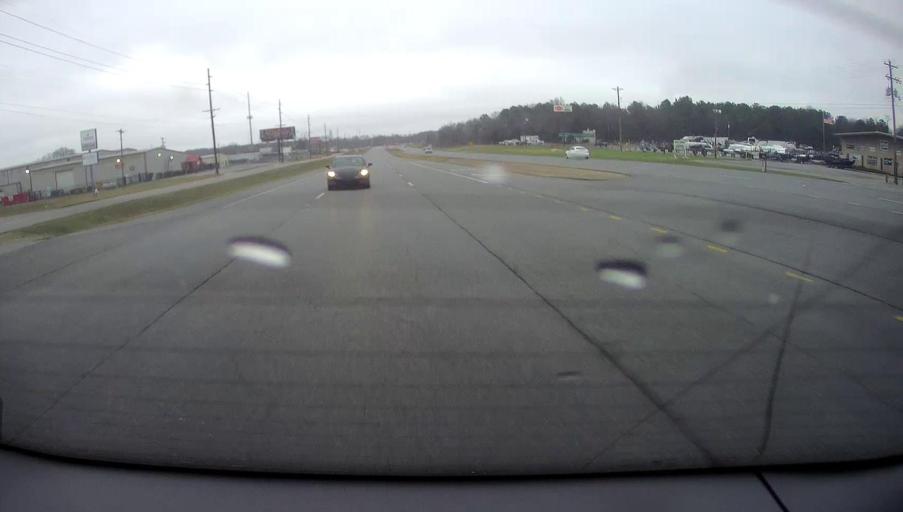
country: US
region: Alabama
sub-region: Morgan County
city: Decatur
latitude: 34.6118
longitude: -87.0312
